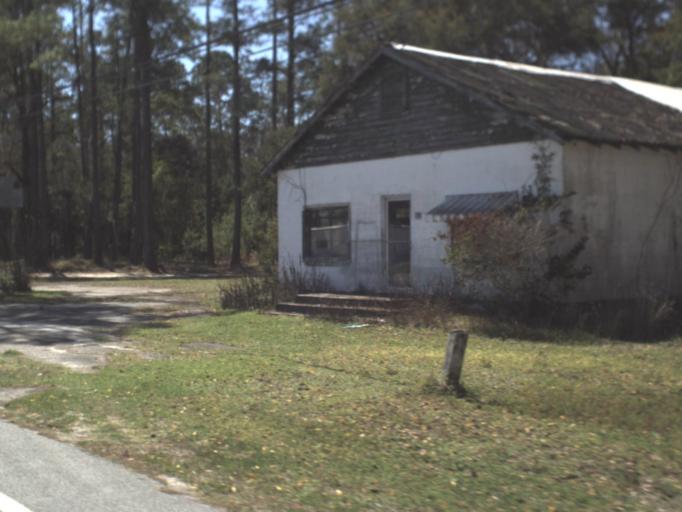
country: US
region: Florida
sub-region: Leon County
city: Woodville
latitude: 30.1668
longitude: -84.2079
